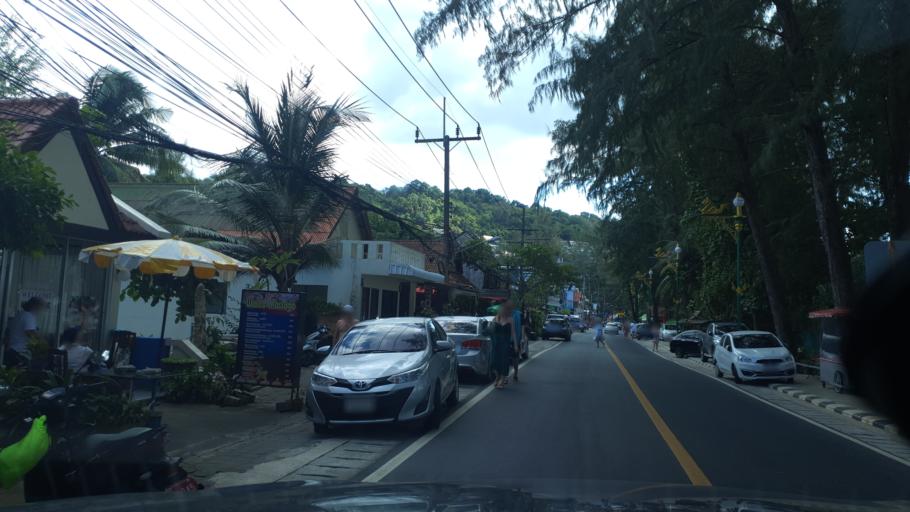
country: TH
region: Phuket
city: Thalang
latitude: 8.0596
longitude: 98.2779
